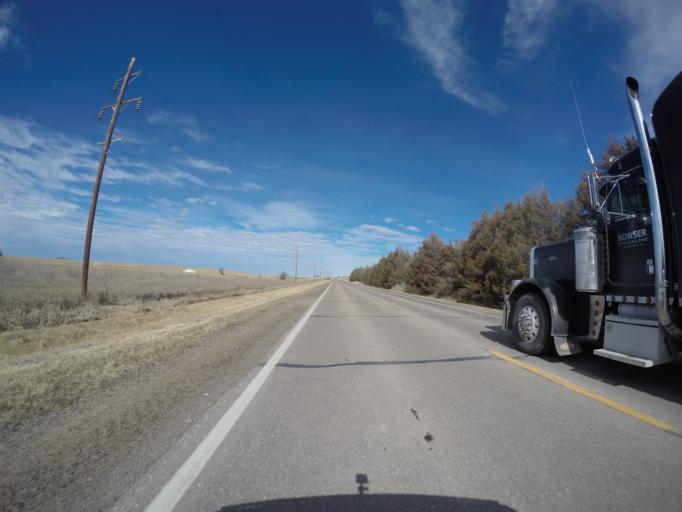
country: US
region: Nebraska
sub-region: Franklin County
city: Franklin
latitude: 40.1081
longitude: -98.9524
